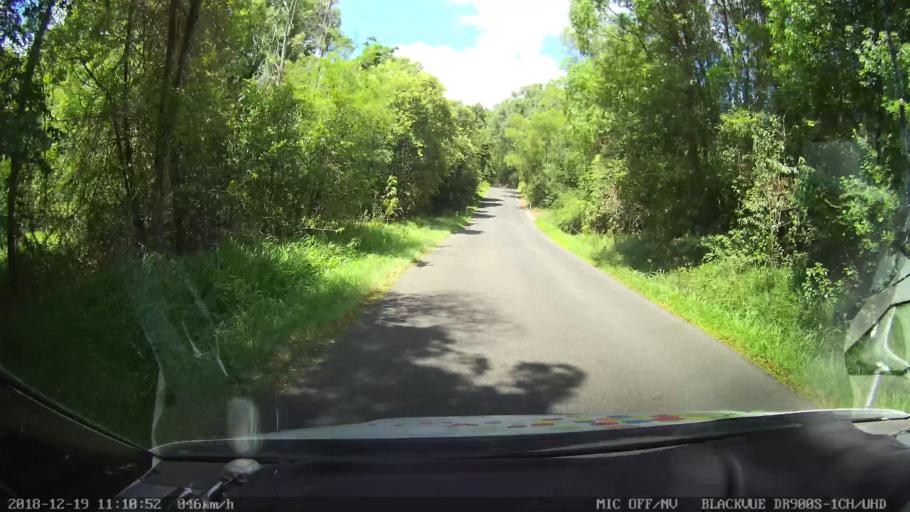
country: AU
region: New South Wales
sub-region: Lismore Municipality
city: Nimbin
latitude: -28.6406
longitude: 153.2596
